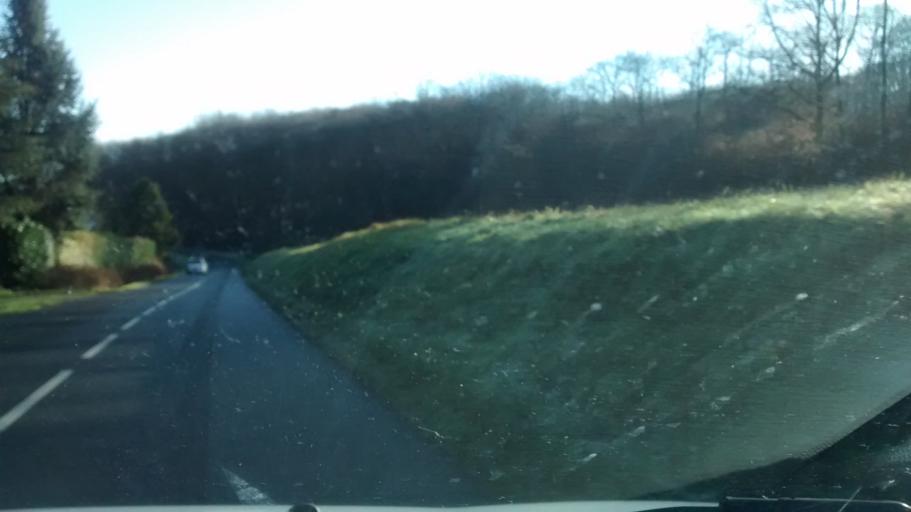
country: FR
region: Centre
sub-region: Departement d'Indre-et-Loire
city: Reugny
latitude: 47.4825
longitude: 0.8735
